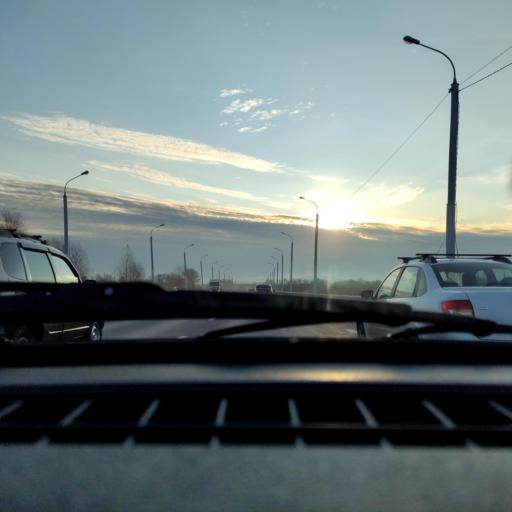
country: RU
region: Bashkortostan
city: Ufa
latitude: 54.8037
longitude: 56.1845
